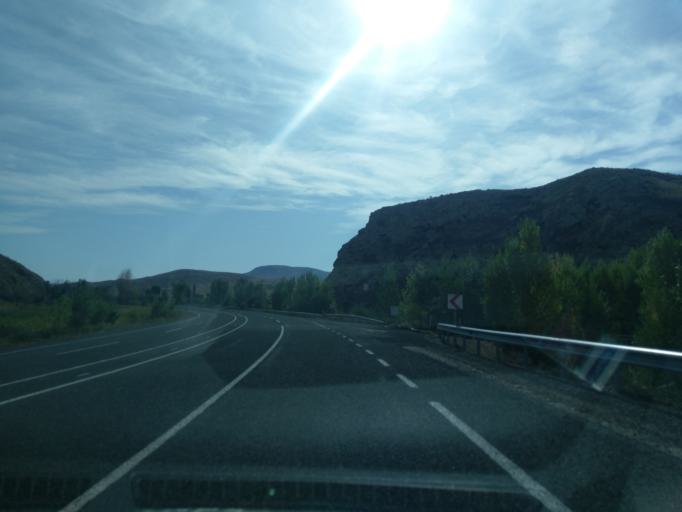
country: TR
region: Sivas
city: Zara
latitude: 39.8491
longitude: 37.8438
